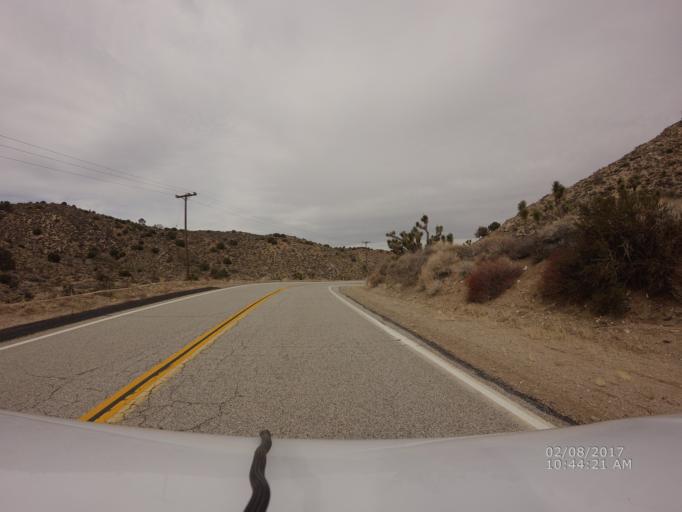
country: US
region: California
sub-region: San Bernardino County
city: Pinon Hills
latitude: 34.4329
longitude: -117.7683
